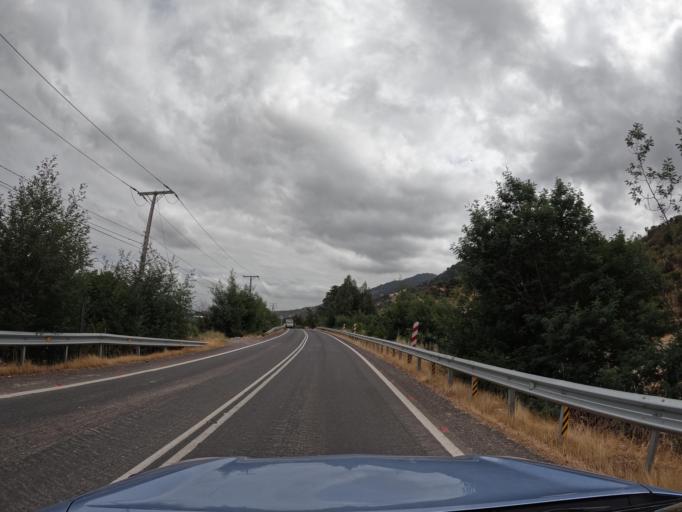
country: CL
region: Maule
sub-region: Provincia de Curico
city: Teno
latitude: -34.8170
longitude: -71.2114
